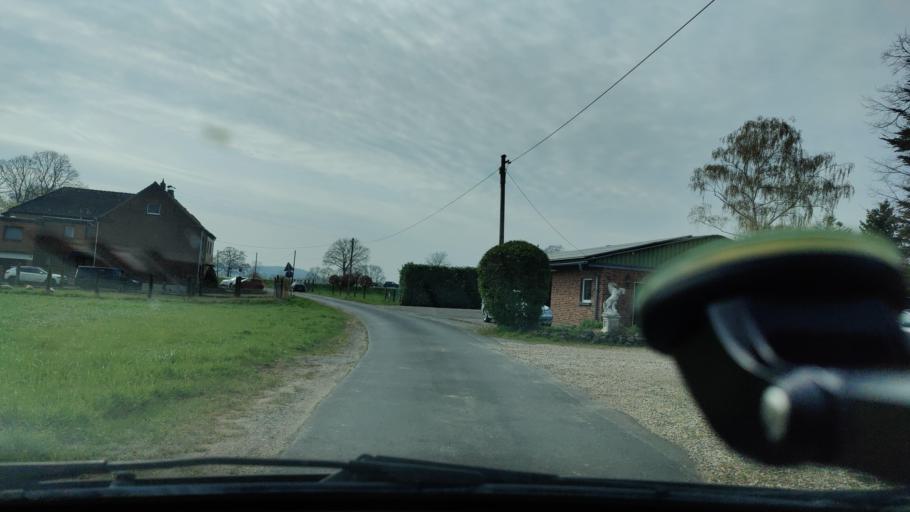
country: DE
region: North Rhine-Westphalia
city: Rheinberg
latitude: 51.5116
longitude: 6.6161
